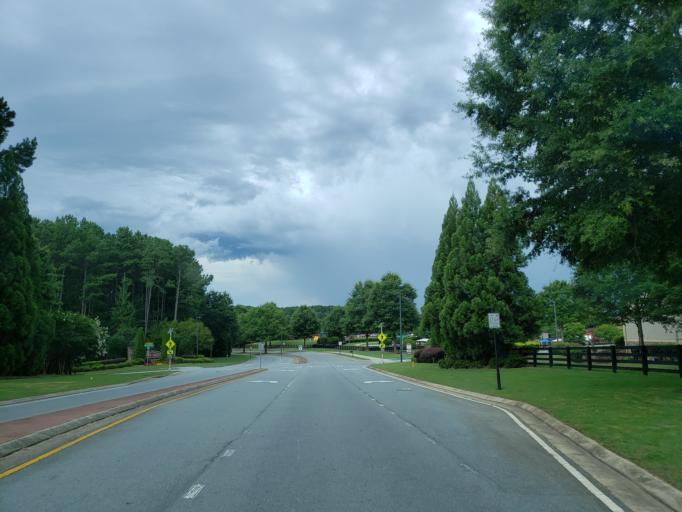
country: US
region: Georgia
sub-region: Bartow County
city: Emerson
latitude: 34.0259
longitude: -84.7816
